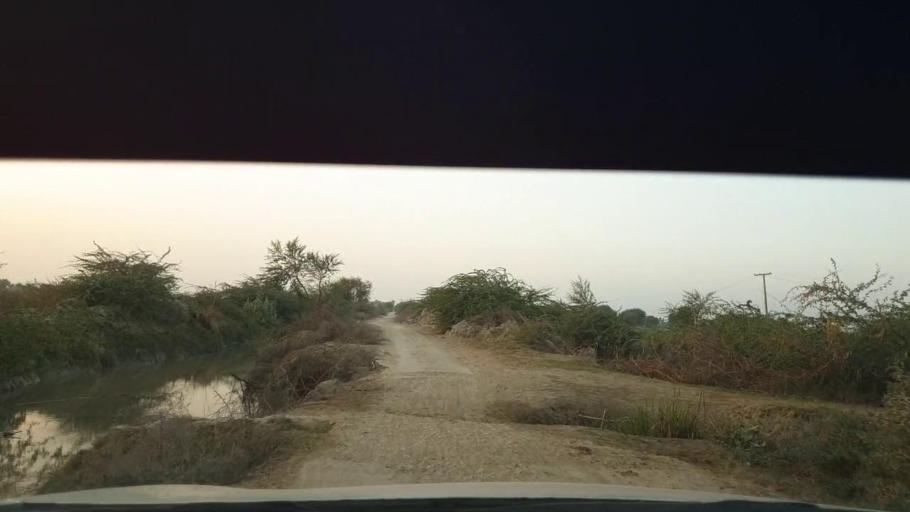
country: PK
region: Sindh
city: Berani
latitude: 25.7749
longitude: 68.9745
